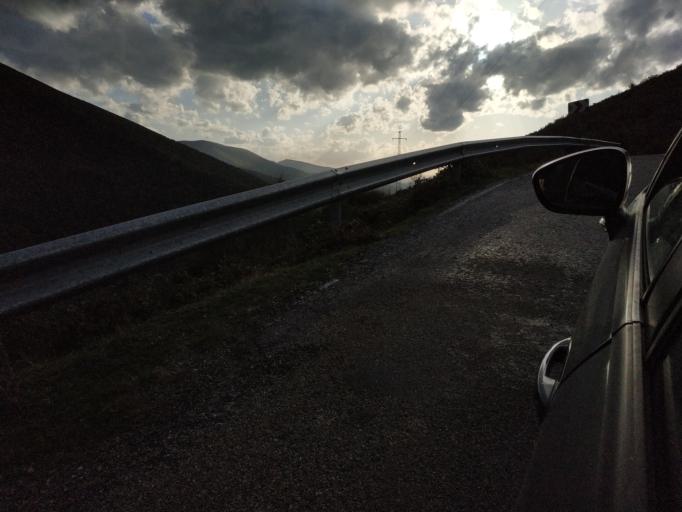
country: ES
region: Castille and Leon
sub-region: Provincia de Leon
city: Candin
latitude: 42.8710
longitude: -6.8357
